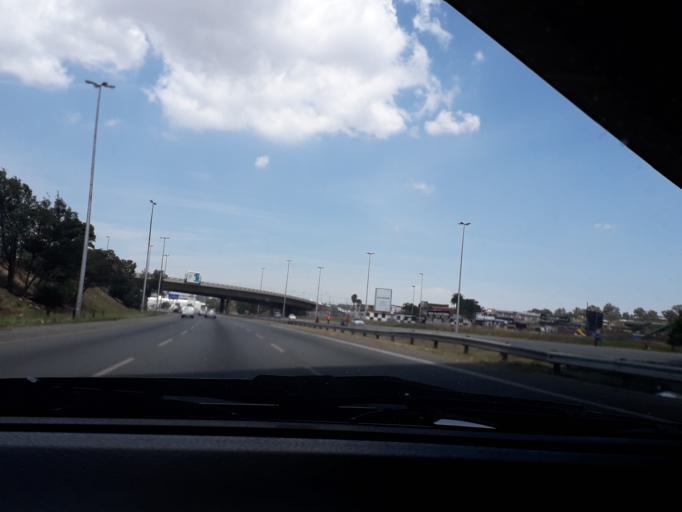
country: ZA
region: Gauteng
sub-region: City of Johannesburg Metropolitan Municipality
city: Johannesburg
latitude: -26.2564
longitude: 27.9898
